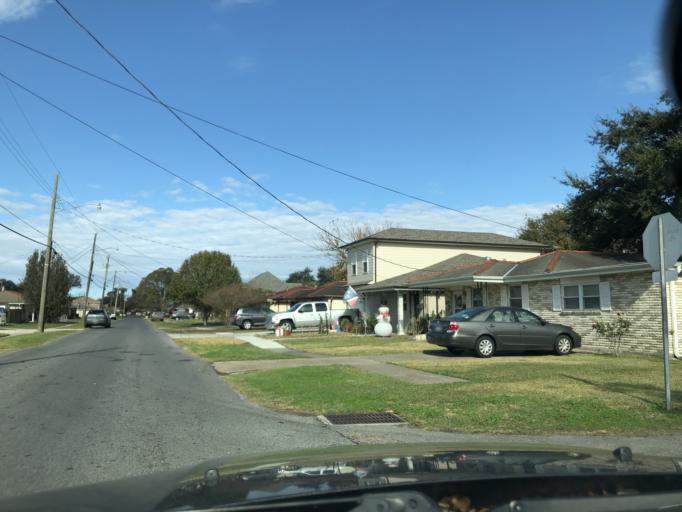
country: US
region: Louisiana
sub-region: Jefferson Parish
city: Metairie Terrace
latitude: 29.9842
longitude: -90.1672
